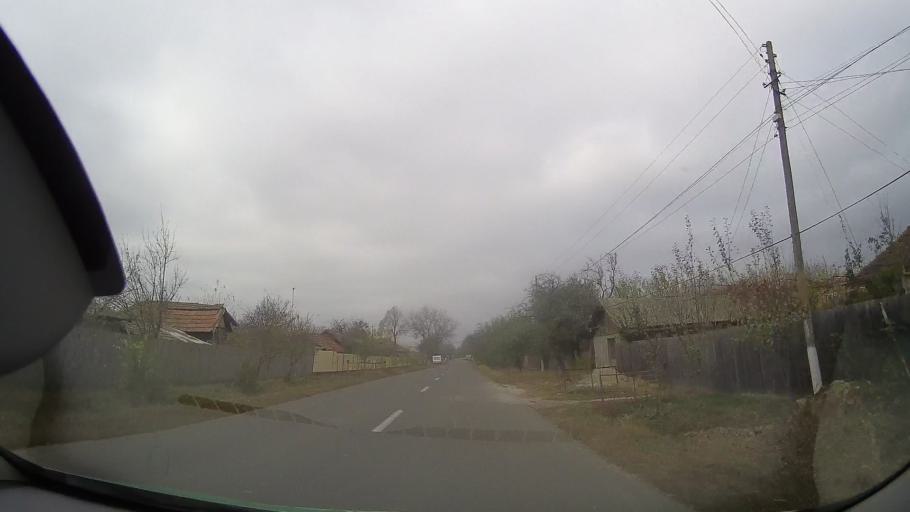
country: RO
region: Buzau
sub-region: Comuna Scutelnici
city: Scutelnici
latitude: 44.8773
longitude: 26.8803
